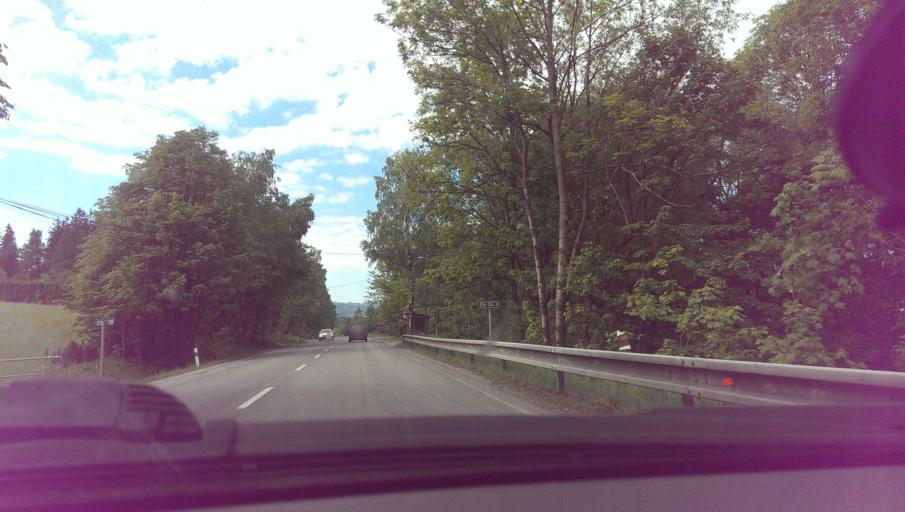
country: CZ
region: Zlin
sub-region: Okres Vsetin
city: Roznov pod Radhostem
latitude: 49.4779
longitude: 18.1657
